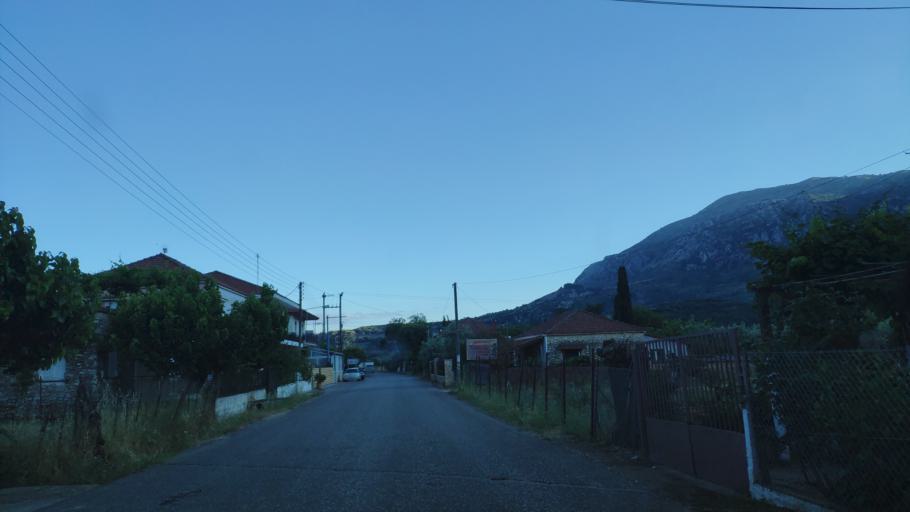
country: GR
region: West Greece
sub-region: Nomos Aitolias kai Akarnanias
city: Astakos
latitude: 38.5841
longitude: 21.0896
